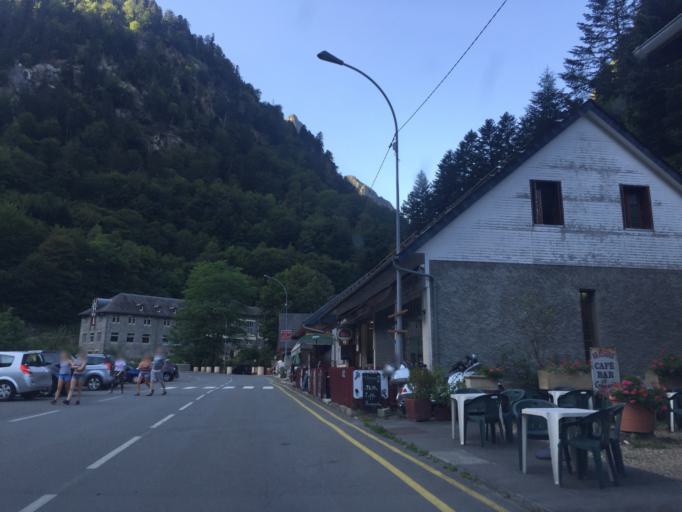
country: FR
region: Midi-Pyrenees
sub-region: Departement des Hautes-Pyrenees
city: Cauterets
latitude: 42.8731
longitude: -0.1094
